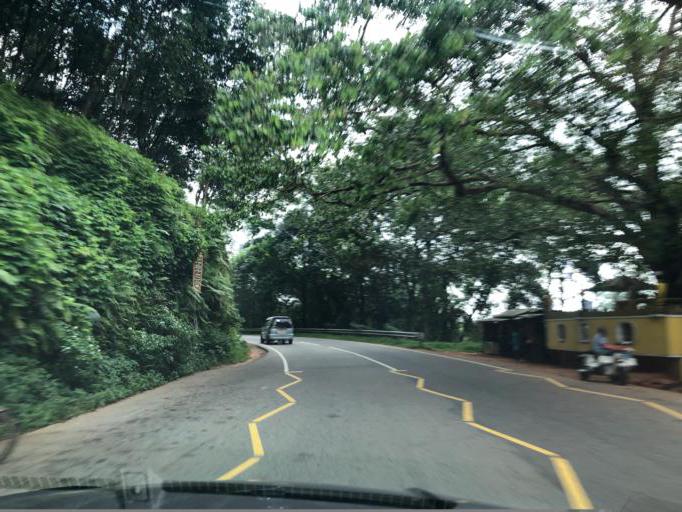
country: LK
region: Western
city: Horana South
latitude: 6.6783
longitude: 80.1262
